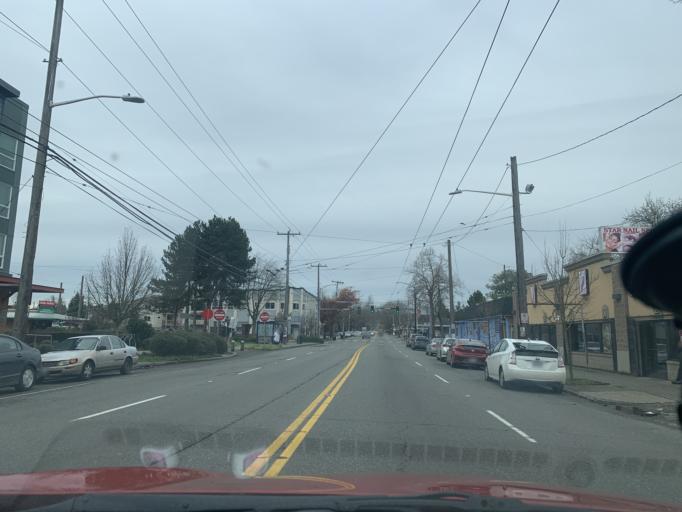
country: US
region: Washington
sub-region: King County
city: Bryn Mawr-Skyway
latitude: 47.5300
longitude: -122.2701
